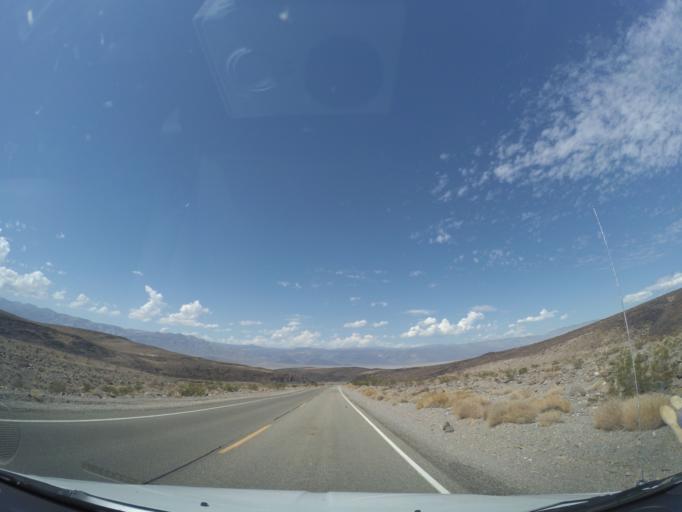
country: US
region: California
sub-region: San Bernardino County
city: Searles Valley
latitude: 36.3483
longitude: -117.3302
